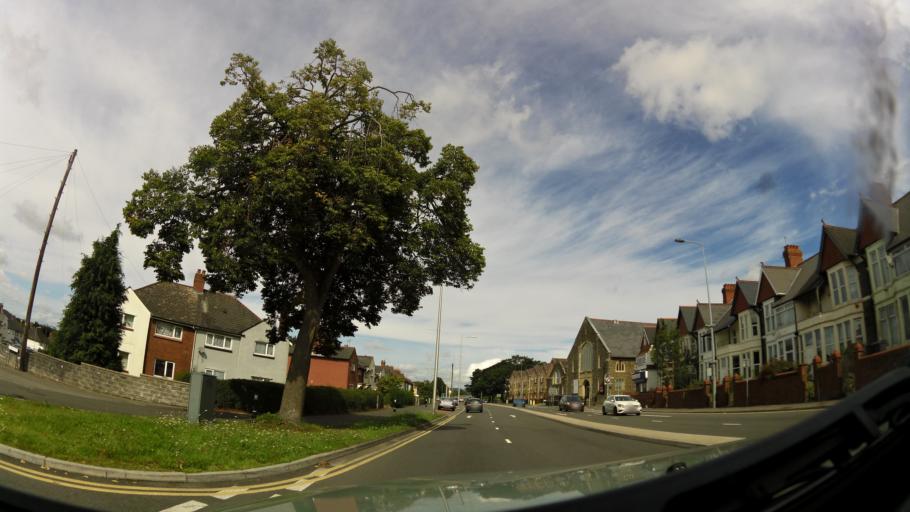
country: GB
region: Wales
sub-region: Cardiff
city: Cardiff
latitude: 51.4993
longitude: -3.1943
